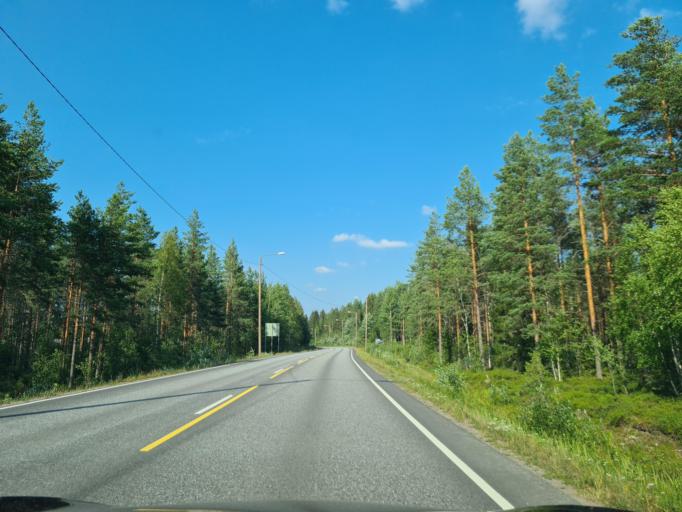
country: FI
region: Satakunta
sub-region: Pohjois-Satakunta
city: Karvia
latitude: 62.0803
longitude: 22.5192
